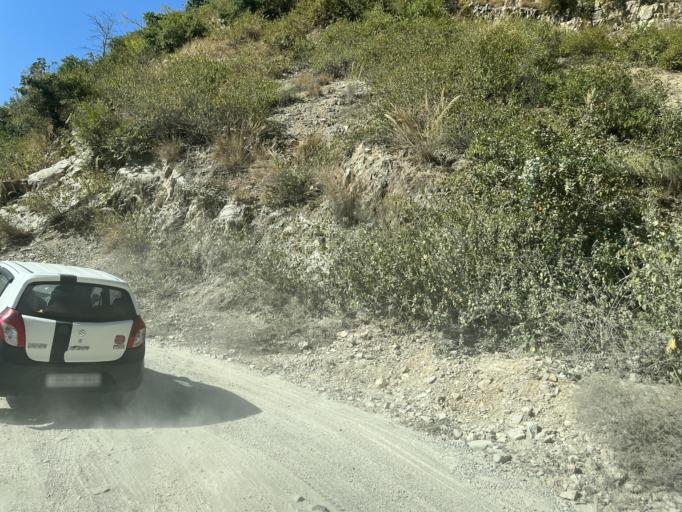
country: IN
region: Uttarakhand
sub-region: Naini Tal
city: Naini Tal
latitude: 29.5116
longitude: 79.4733
